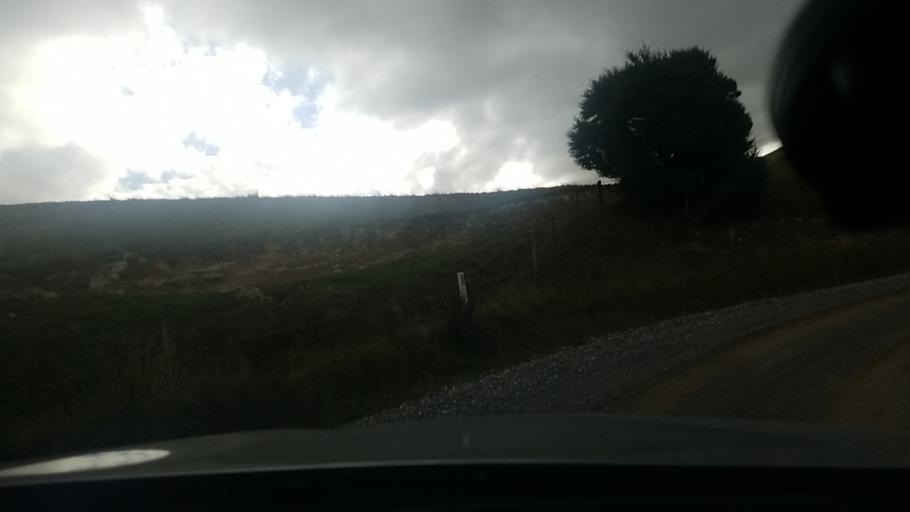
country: NZ
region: Marlborough
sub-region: Marlborough District
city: Blenheim
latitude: -41.5870
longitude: 174.0869
